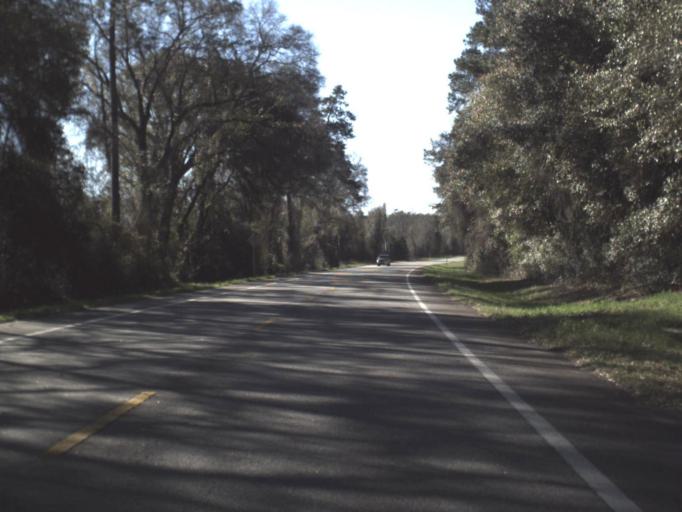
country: US
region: Georgia
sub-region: Brooks County
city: Quitman
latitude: 30.5834
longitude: -83.6377
